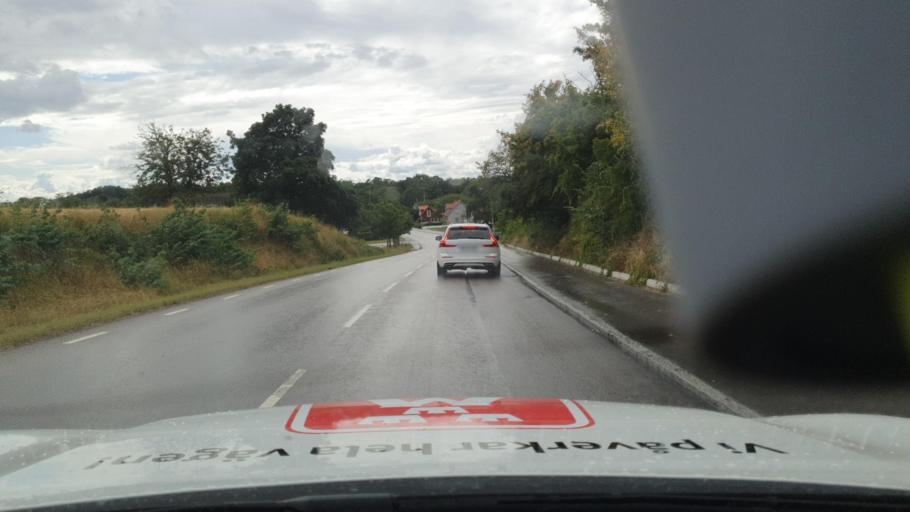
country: SE
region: Skane
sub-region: Angelholms Kommun
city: Vejbystrand
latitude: 56.4314
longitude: 12.6484
